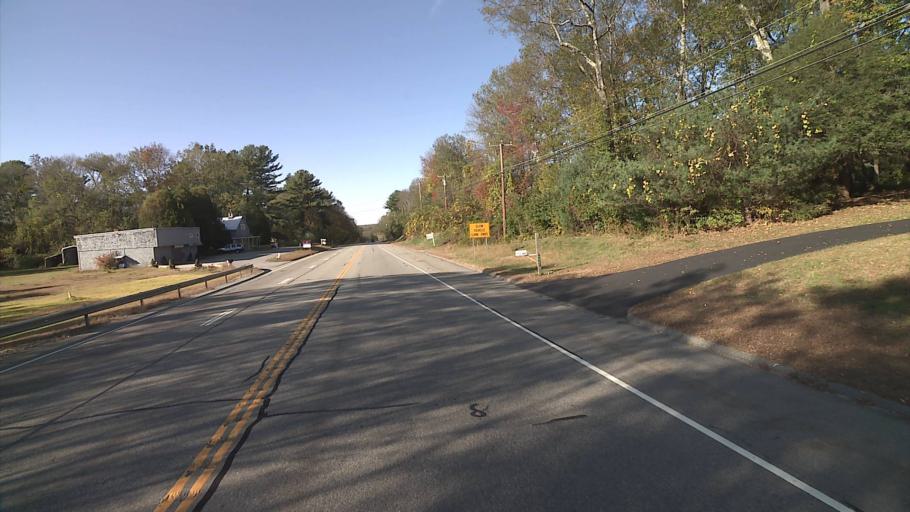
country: US
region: Connecticut
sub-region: Windham County
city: Wauregan
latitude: 41.7814
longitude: -72.0222
